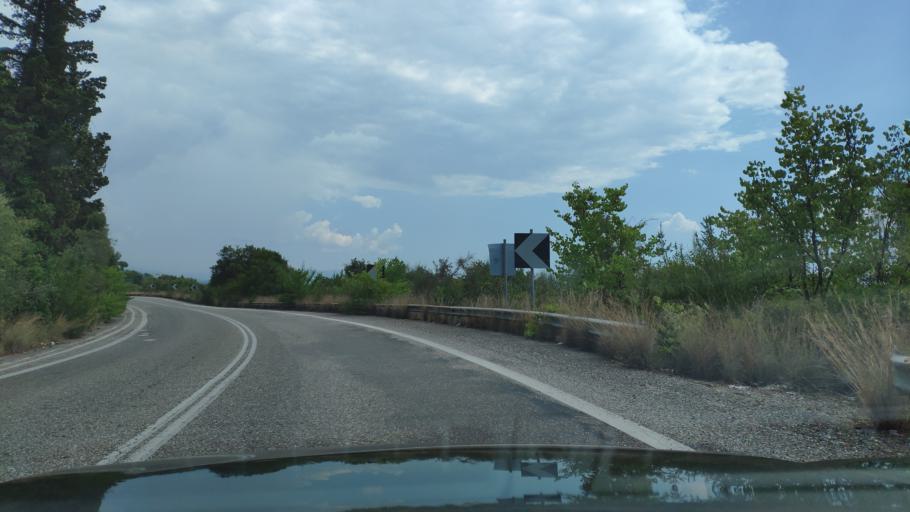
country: GR
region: West Greece
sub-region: Nomos Aitolias kai Akarnanias
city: Menidi
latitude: 39.0018
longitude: 21.1485
